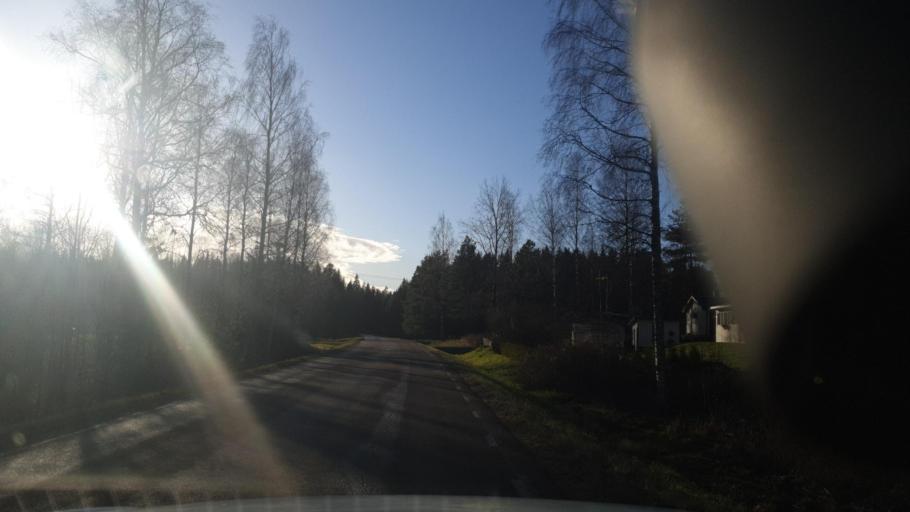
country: SE
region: Vaermland
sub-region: Eda Kommun
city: Amotfors
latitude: 59.8688
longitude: 12.4996
